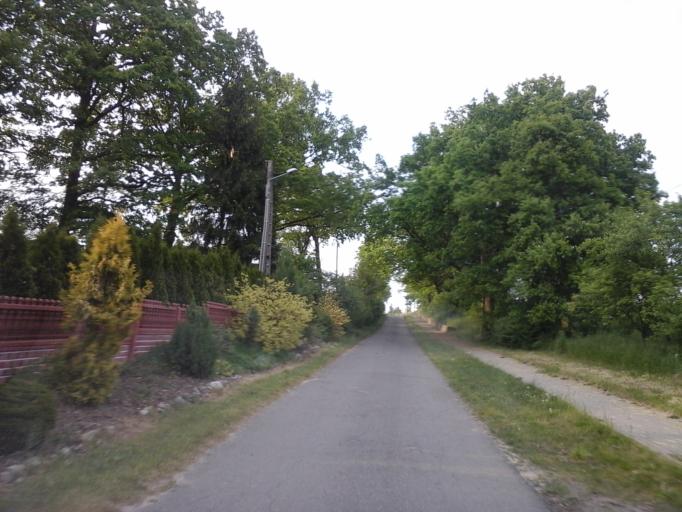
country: PL
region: West Pomeranian Voivodeship
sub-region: Powiat choszczenski
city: Pelczyce
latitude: 52.9858
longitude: 15.3738
